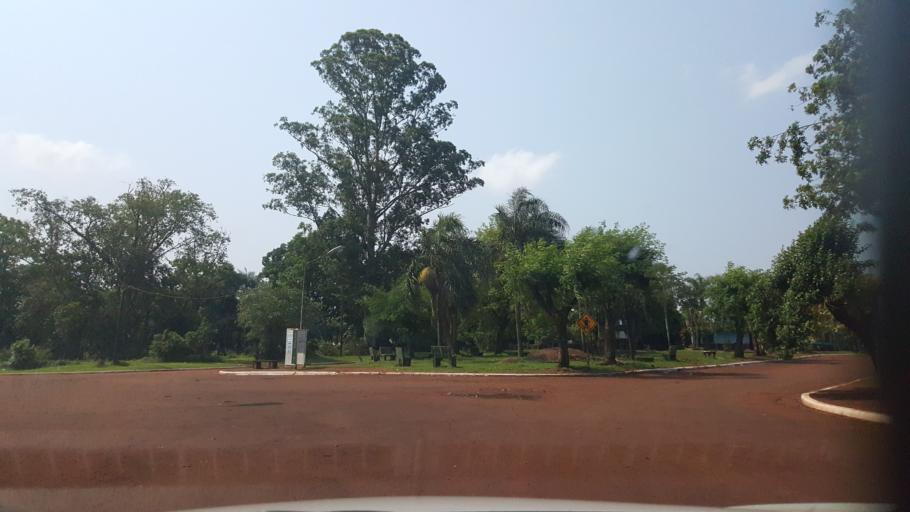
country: AR
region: Misiones
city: Santa Ana
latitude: -27.3691
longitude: -55.5811
